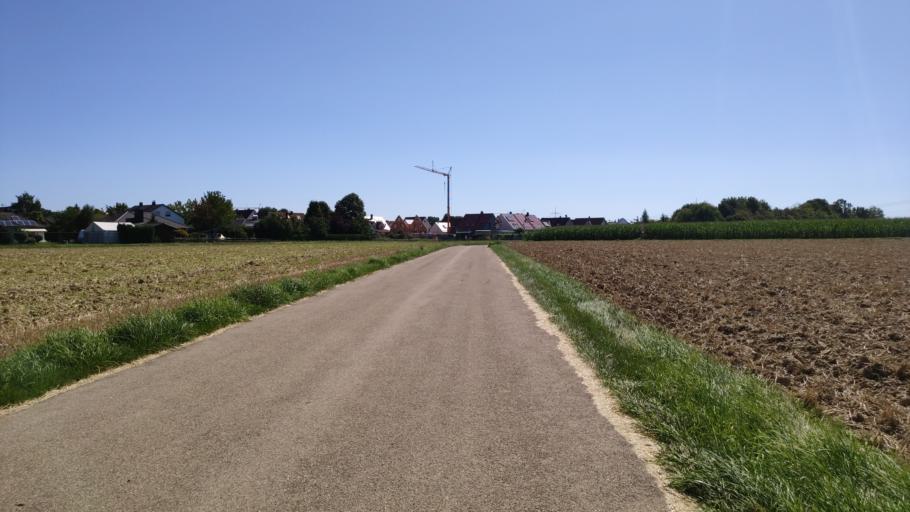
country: DE
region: Bavaria
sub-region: Swabia
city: Oberottmarshausen
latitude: 48.2380
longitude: 10.8485
